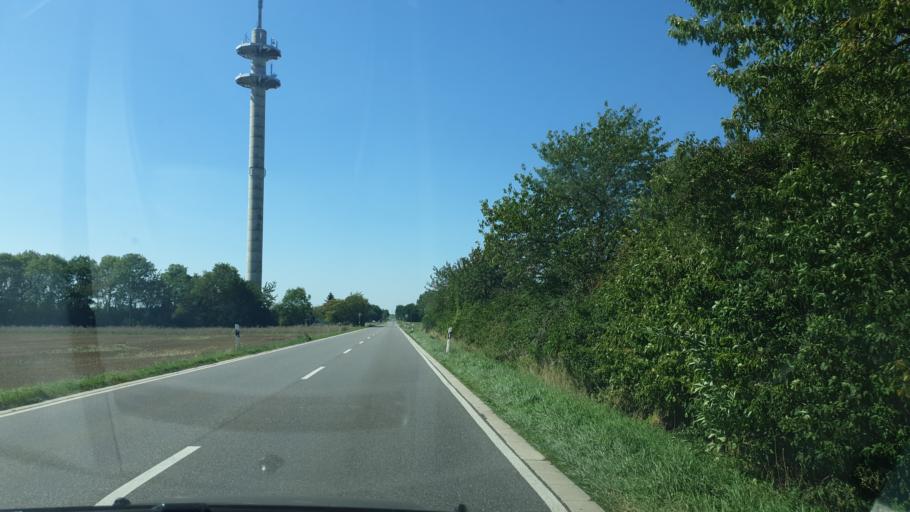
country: DE
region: North Rhine-Westphalia
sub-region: Regierungsbezirk Koln
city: Euskirchen
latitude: 50.6804
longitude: 6.8062
